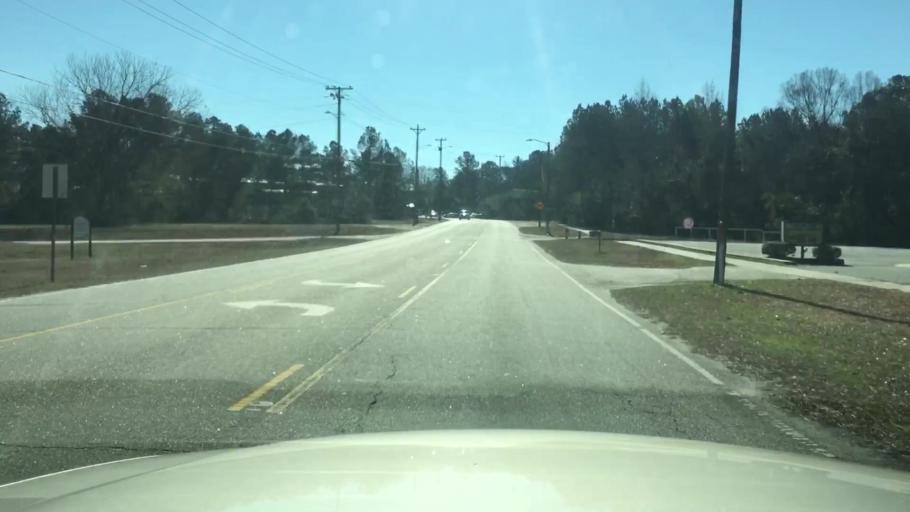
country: US
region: North Carolina
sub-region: Cumberland County
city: Fayetteville
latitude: 35.0397
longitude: -78.8970
